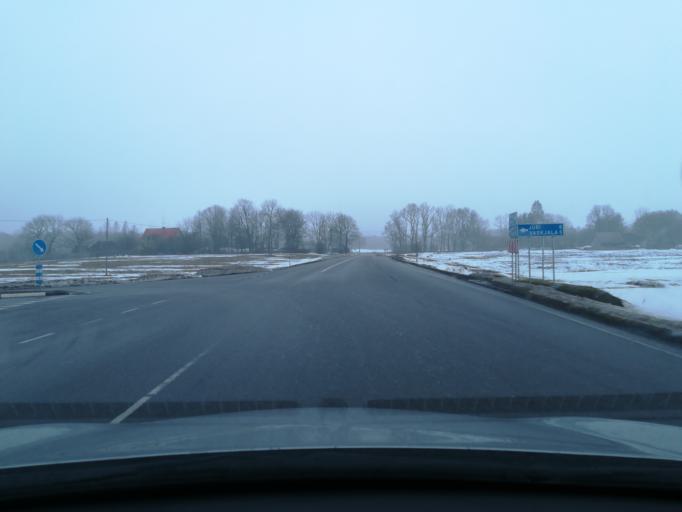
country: EE
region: Harju
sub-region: Raasiku vald
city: Arukula
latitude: 59.3686
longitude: 25.0272
